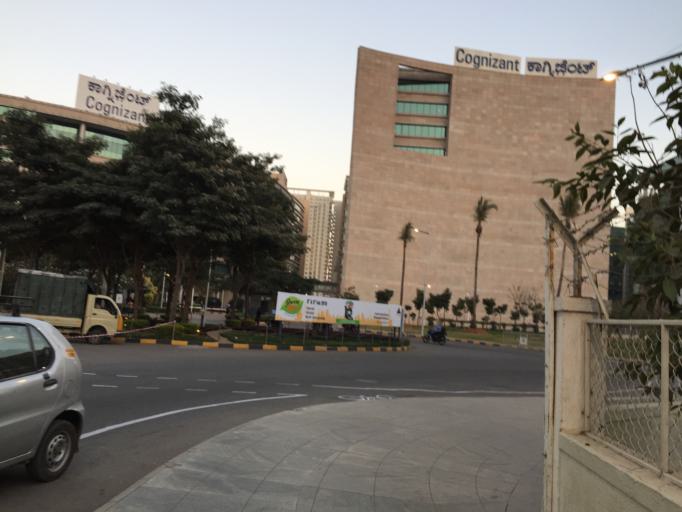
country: IN
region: Karnataka
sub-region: Bangalore Urban
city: Yelahanka
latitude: 13.0502
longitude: 77.6216
